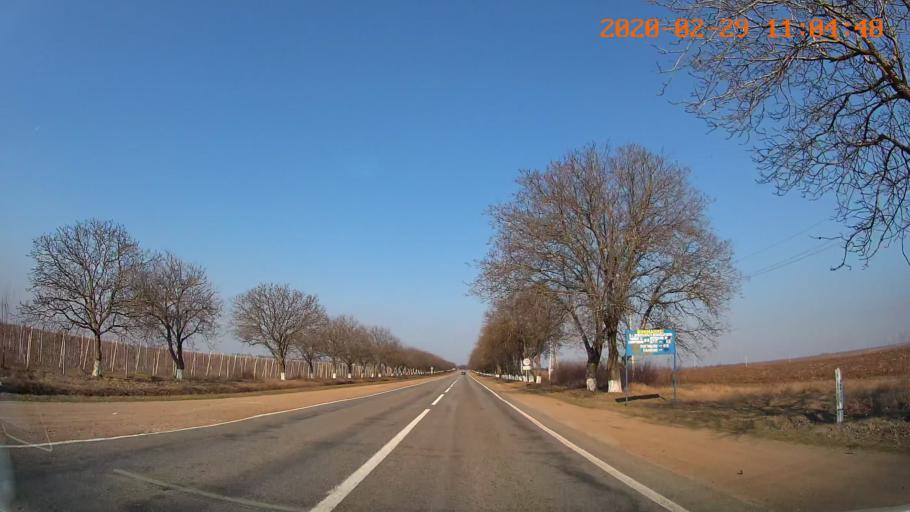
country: MD
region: Criuleni
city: Criuleni
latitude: 47.1939
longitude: 29.1980
